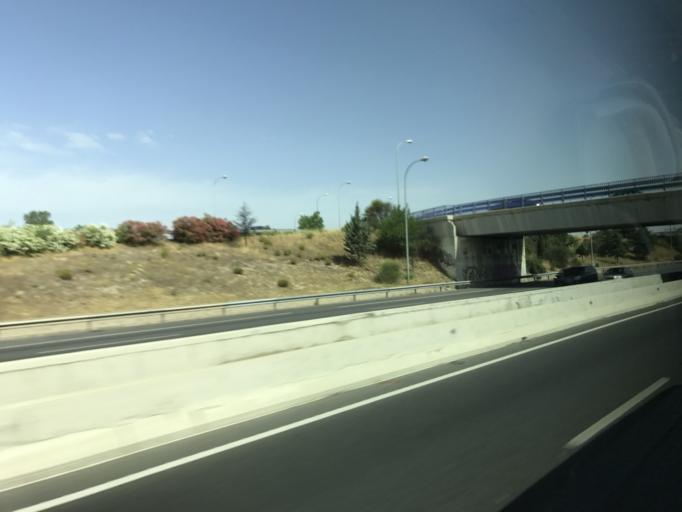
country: ES
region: Madrid
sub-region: Provincia de Madrid
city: San Blas
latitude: 40.4288
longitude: -3.5971
